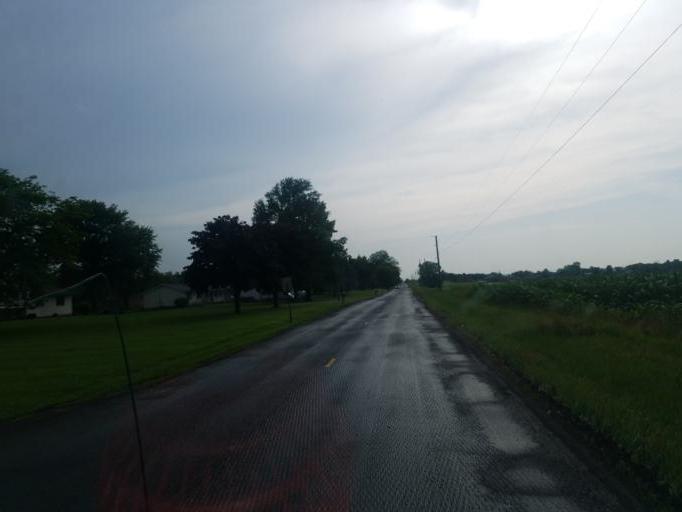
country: US
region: Ohio
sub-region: Wayne County
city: West Salem
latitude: 40.9229
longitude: -82.0766
